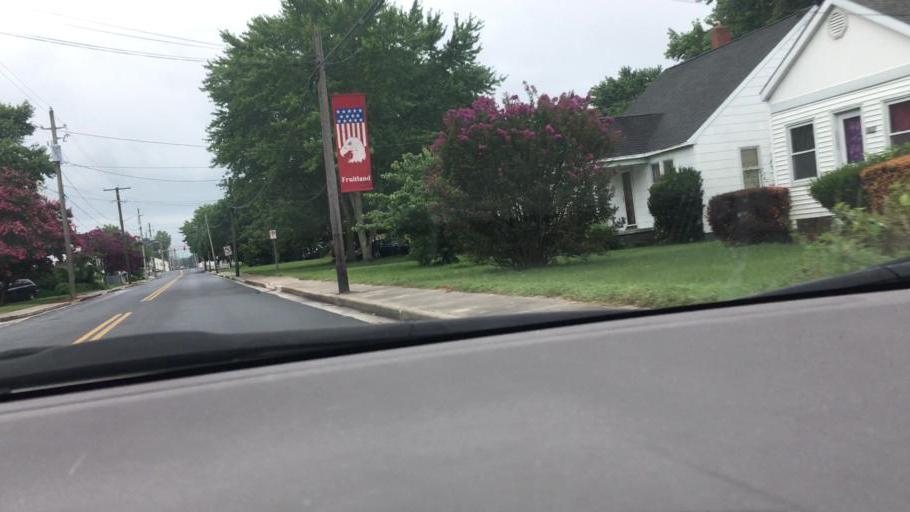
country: US
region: Maryland
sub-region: Wicomico County
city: Fruitland
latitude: 38.3242
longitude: -75.6212
